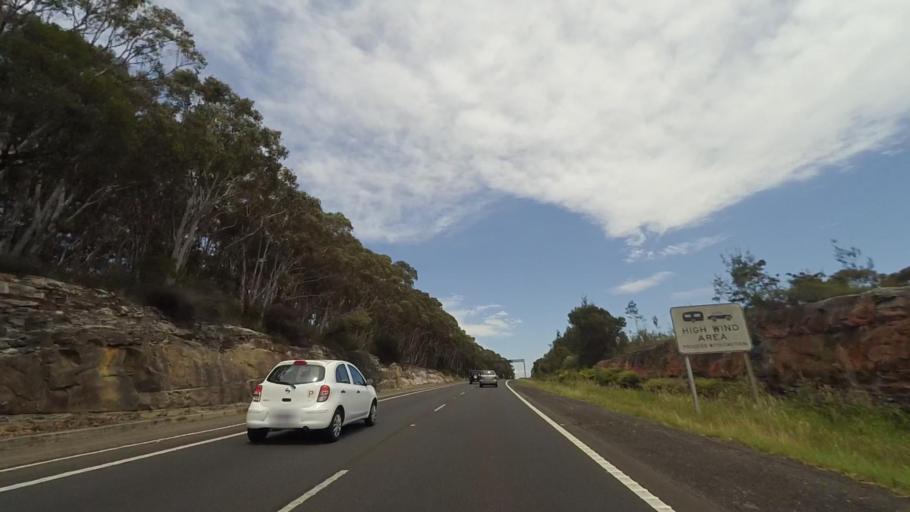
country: AU
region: New South Wales
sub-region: Wollongong
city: Helensburgh
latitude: -34.2435
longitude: 150.9425
